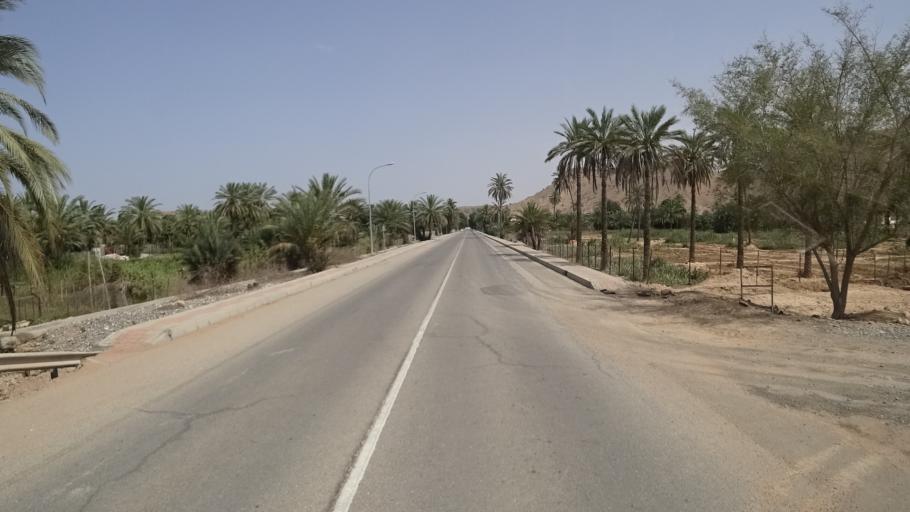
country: OM
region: Muhafazat Masqat
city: Muscat
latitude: 23.1717
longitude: 58.9148
